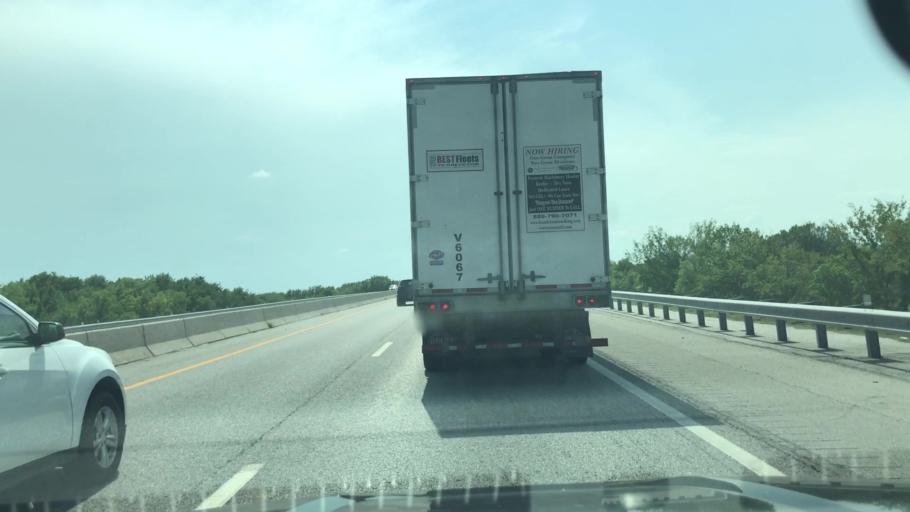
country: US
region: Oklahoma
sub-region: Ottawa County
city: Afton
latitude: 36.7179
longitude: -94.9482
